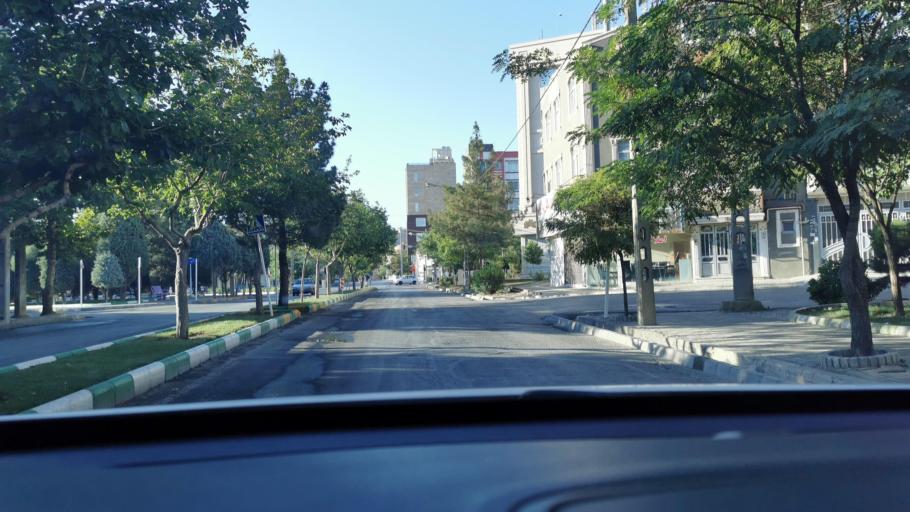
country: IR
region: Razavi Khorasan
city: Mashhad
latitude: 36.3594
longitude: 59.4908
